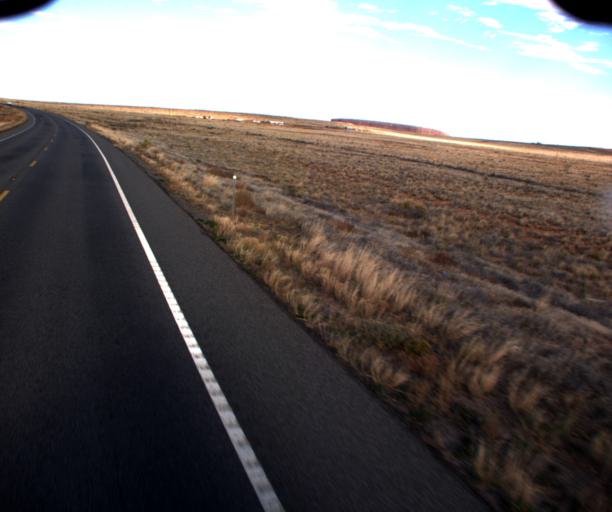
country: US
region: Arizona
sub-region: Apache County
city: Lukachukai
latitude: 36.9573
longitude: -109.3047
